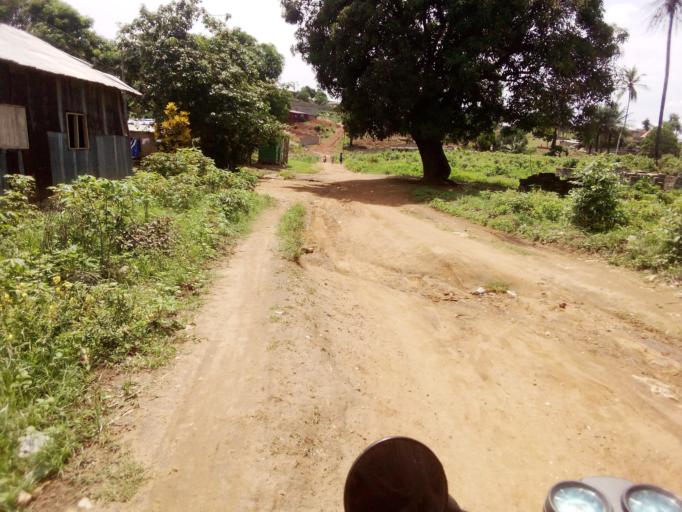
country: SL
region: Western Area
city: Waterloo
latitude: 8.3440
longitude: -13.0726
